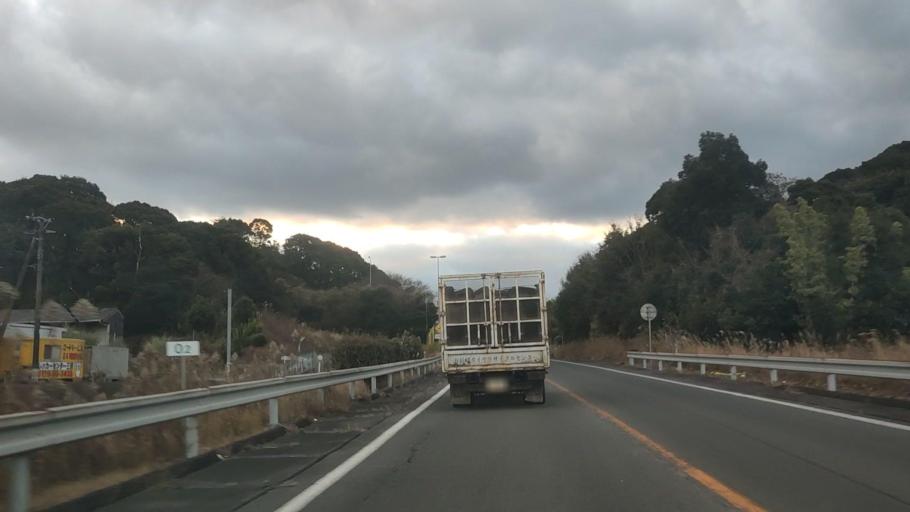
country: JP
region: Nagasaki
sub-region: Isahaya-shi
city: Isahaya
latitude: 32.8158
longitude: 129.9653
